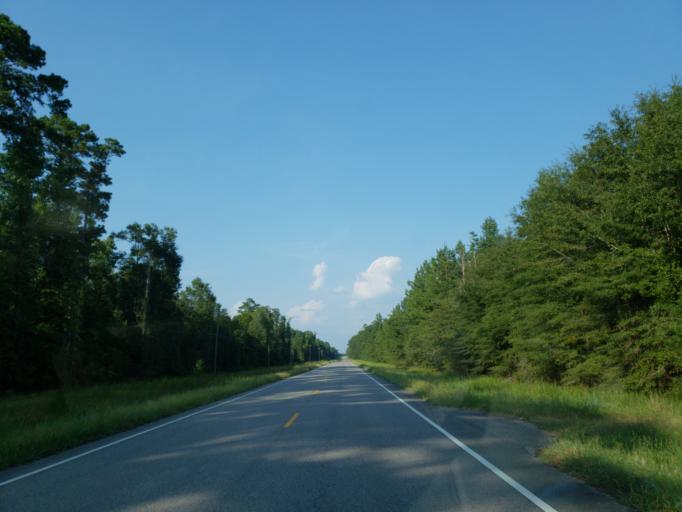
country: US
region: Alabama
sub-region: Sumter County
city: Livingston
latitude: 32.7328
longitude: -88.0586
